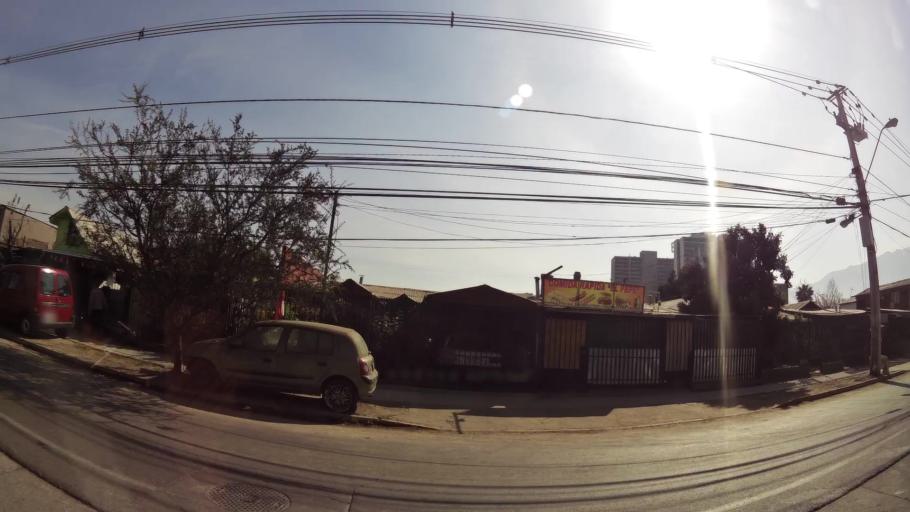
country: CL
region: Santiago Metropolitan
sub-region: Provincia de Santiago
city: Villa Presidente Frei, Nunoa, Santiago, Chile
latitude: -33.4998
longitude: -70.5892
